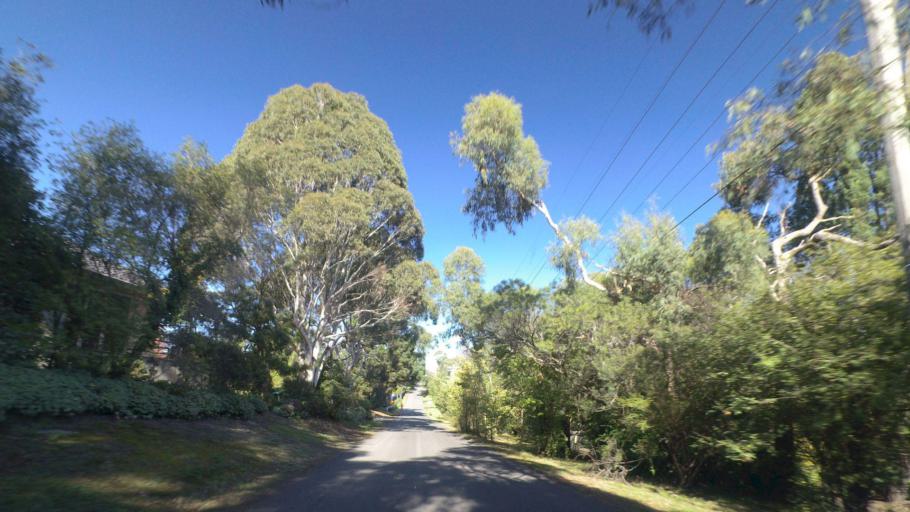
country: AU
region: Victoria
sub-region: Nillumbik
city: Eltham
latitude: -37.7505
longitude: 145.1501
